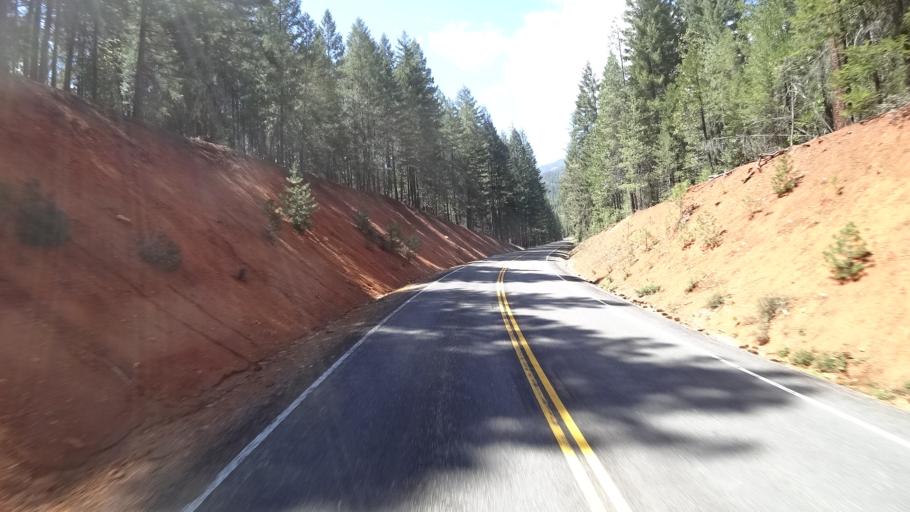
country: US
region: California
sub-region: Trinity County
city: Lewiston
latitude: 40.8460
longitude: -122.8458
